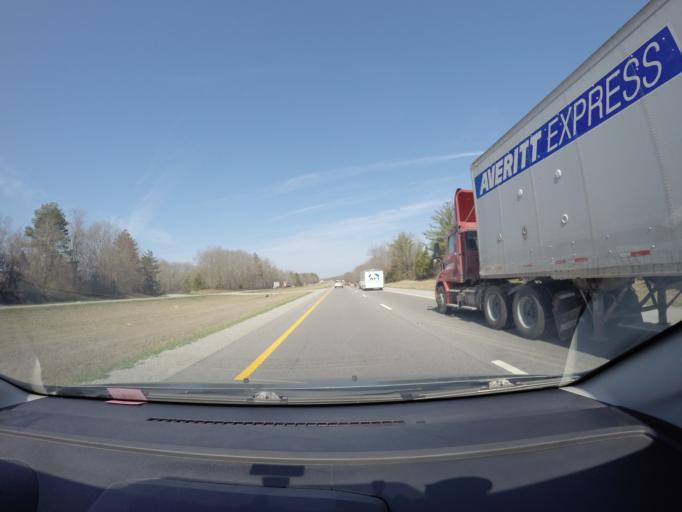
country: US
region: Tennessee
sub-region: Coffee County
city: New Union
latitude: 35.5208
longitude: -86.1291
